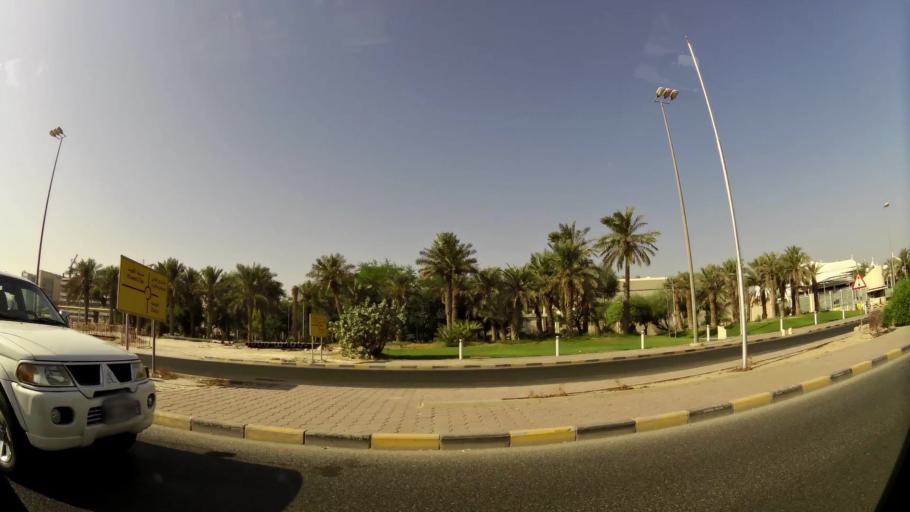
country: KW
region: Al Asimah
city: Ash Shamiyah
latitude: 29.3526
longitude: 47.9448
